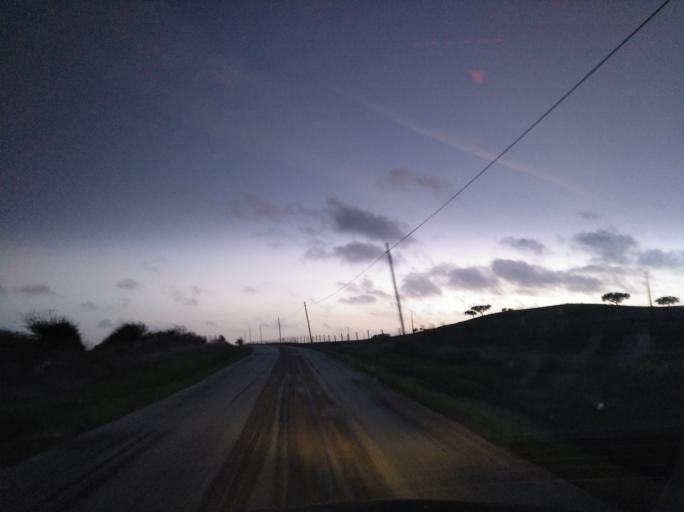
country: PT
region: Portalegre
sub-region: Campo Maior
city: Campo Maior
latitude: 39.0663
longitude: -7.0297
